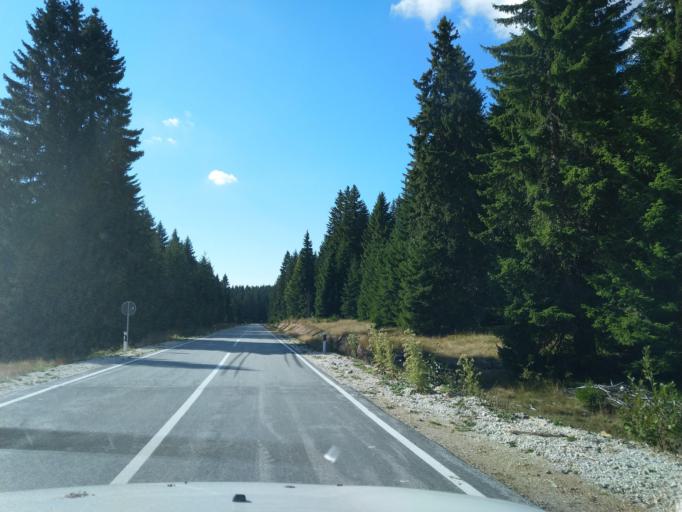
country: RS
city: Sokolovica
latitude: 43.2820
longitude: 20.3306
